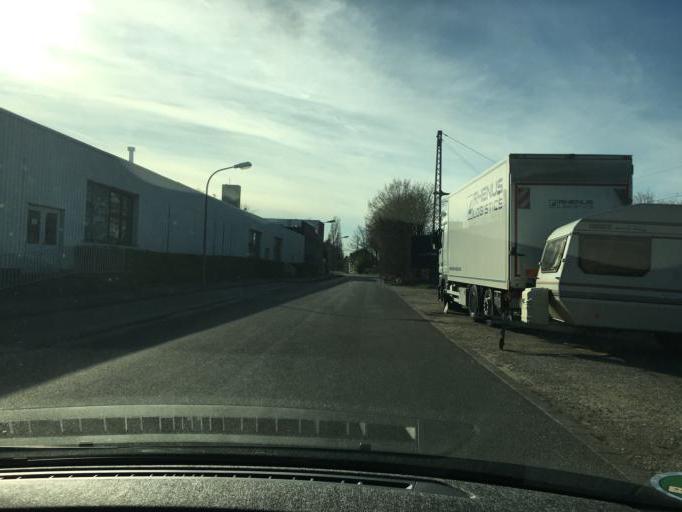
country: DE
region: North Rhine-Westphalia
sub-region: Regierungsbezirk Dusseldorf
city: Korschenbroich
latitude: 51.1958
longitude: 6.5076
